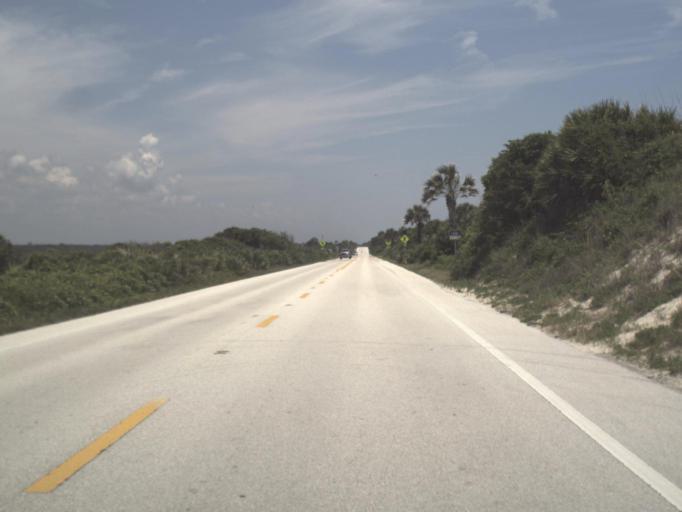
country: US
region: Florida
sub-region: Saint Johns County
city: Palm Valley
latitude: 30.1144
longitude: -81.3451
